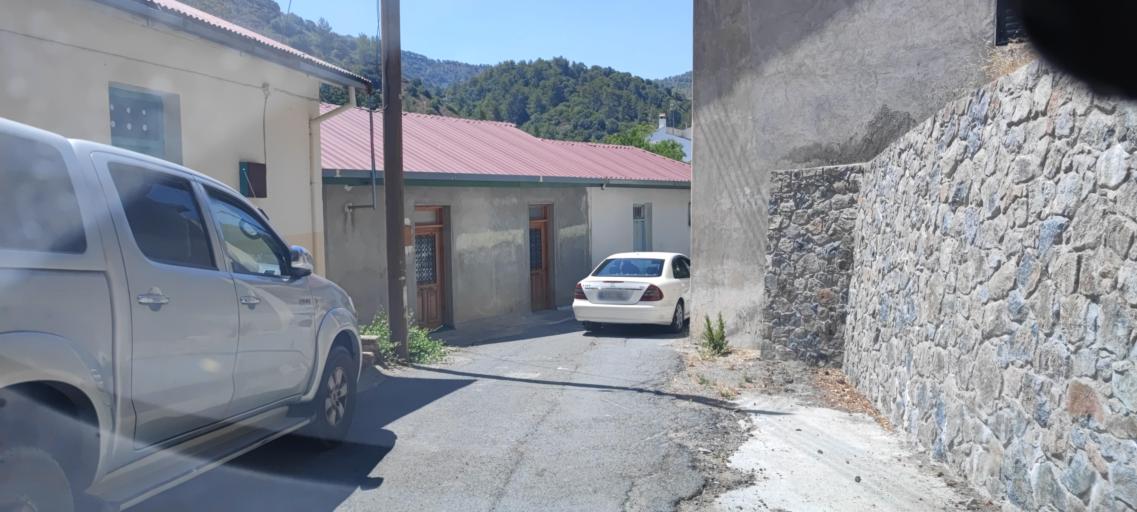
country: CY
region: Lefkosia
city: Kakopetria
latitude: 34.9308
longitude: 32.7943
